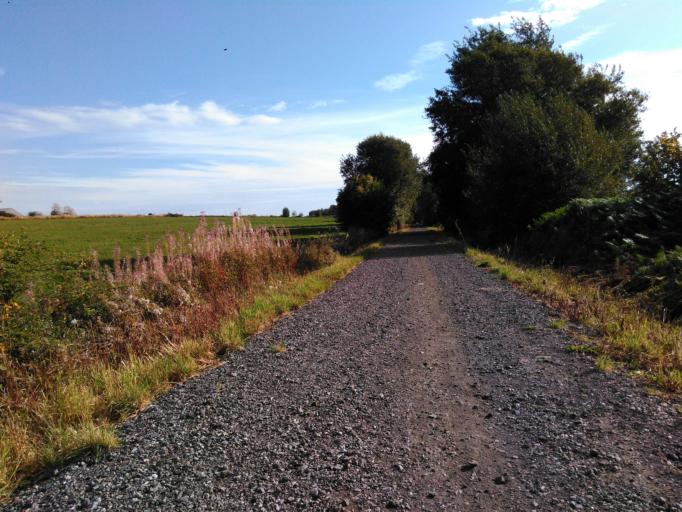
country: BE
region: Wallonia
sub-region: Province du Luxembourg
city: Neufchateau
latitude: 49.9179
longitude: 5.4052
